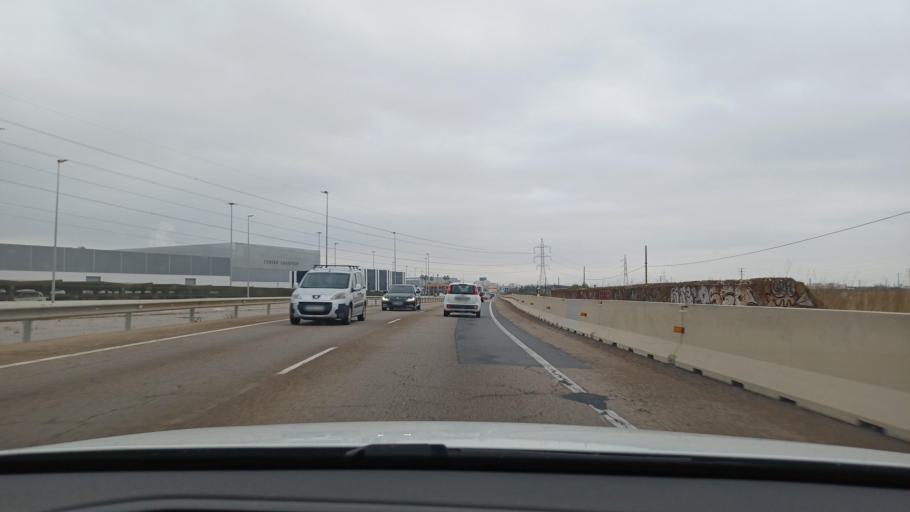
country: ES
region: Valencia
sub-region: Provincia de Castello
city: Vila-real
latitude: 39.9142
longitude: -0.1123
